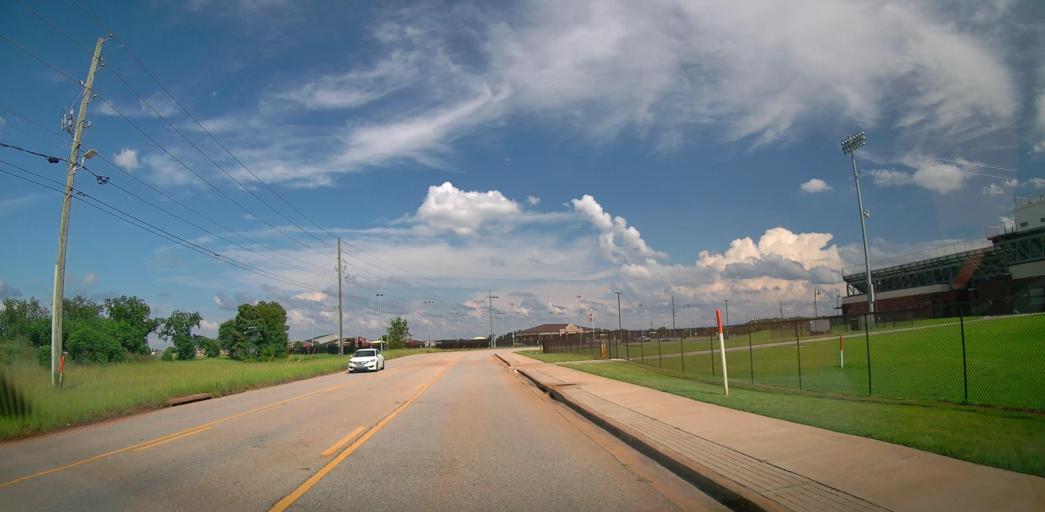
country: US
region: Georgia
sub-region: Houston County
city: Centerville
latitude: 32.5489
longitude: -83.6781
